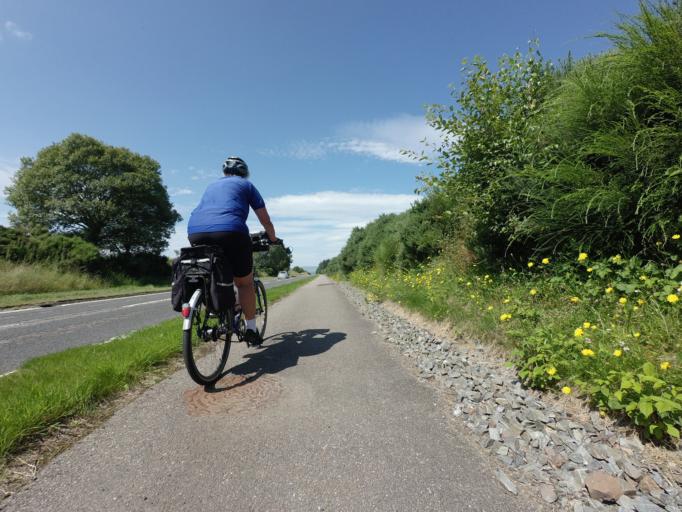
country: GB
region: Scotland
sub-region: Highland
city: Conon Bridge
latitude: 57.5439
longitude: -4.3806
